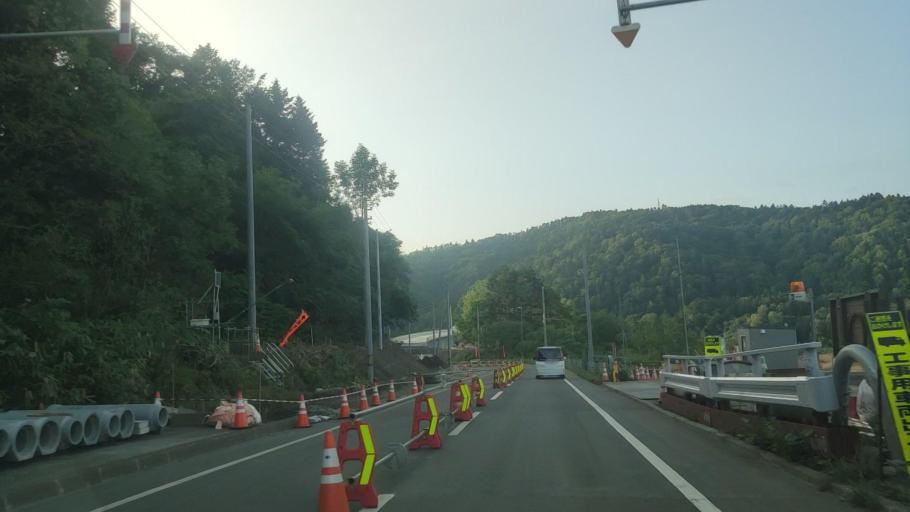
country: JP
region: Hokkaido
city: Bibai
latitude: 43.2320
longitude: 142.0392
